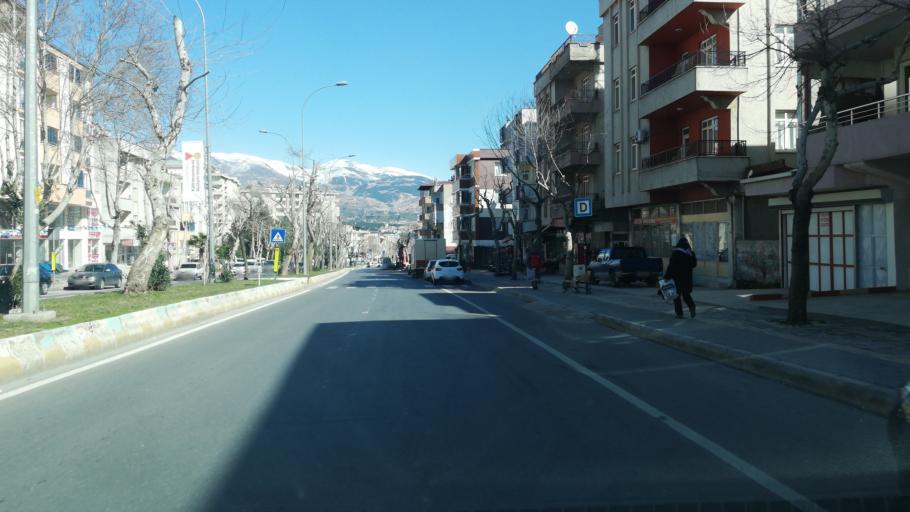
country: TR
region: Kahramanmaras
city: Kahramanmaras
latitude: 37.5873
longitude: 36.9067
